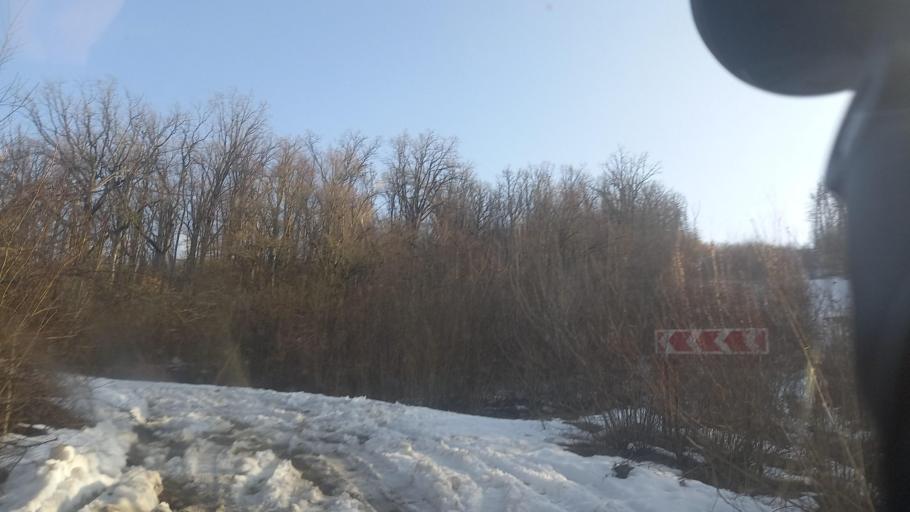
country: RU
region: Krasnodarskiy
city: Smolenskaya
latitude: 44.6691
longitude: 38.7961
